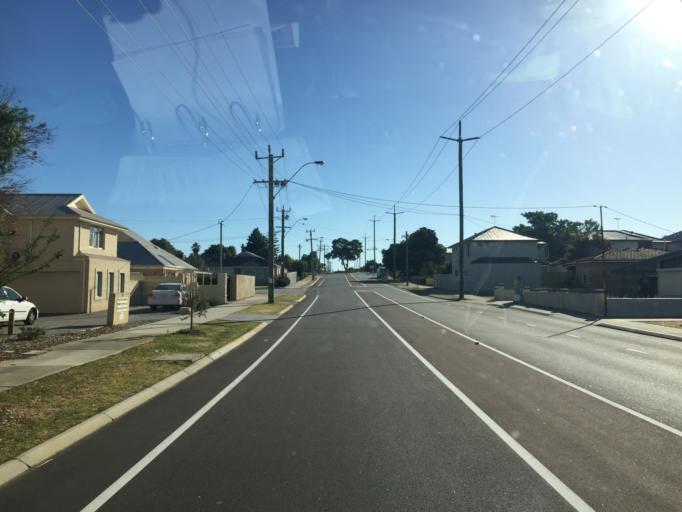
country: AU
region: Western Australia
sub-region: Belmont
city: Rivervale
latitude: -31.9665
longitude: 115.9220
